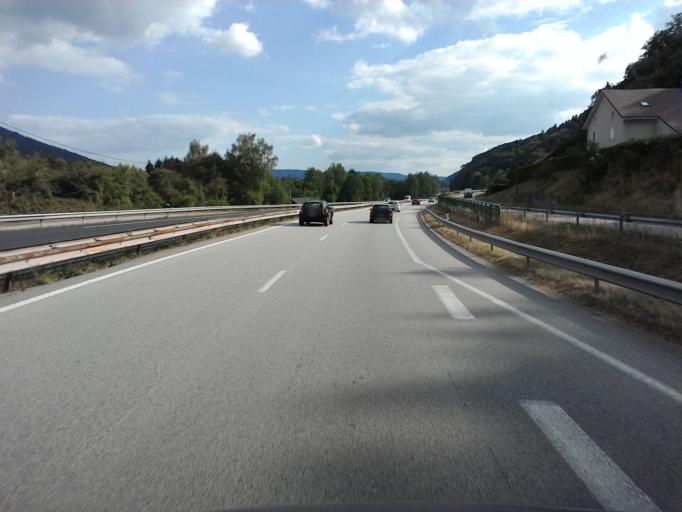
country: FR
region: Lorraine
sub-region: Departement des Vosges
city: Saint-Nabord
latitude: 48.0664
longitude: 6.5974
